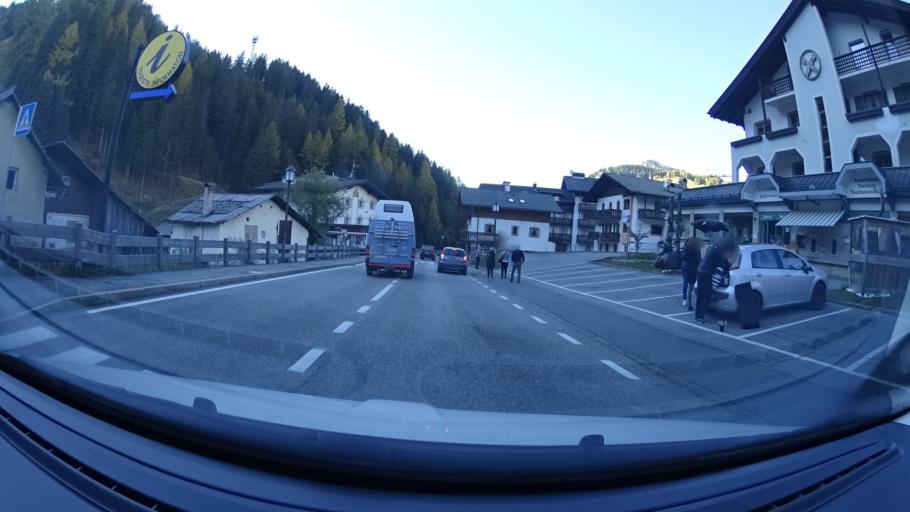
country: IT
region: Trentino-Alto Adige
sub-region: Bolzano
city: Selva
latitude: 46.5538
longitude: 11.7602
